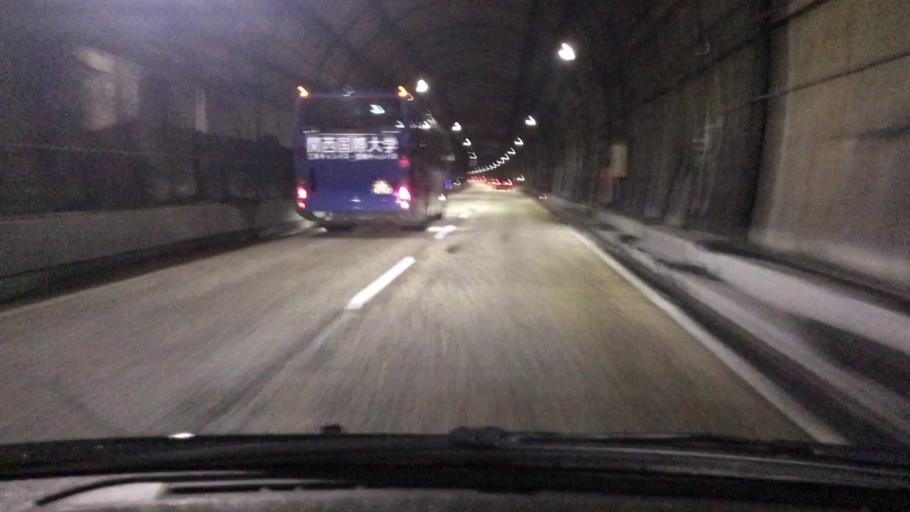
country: JP
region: Hyogo
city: Kobe
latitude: 34.7168
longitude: 135.1884
